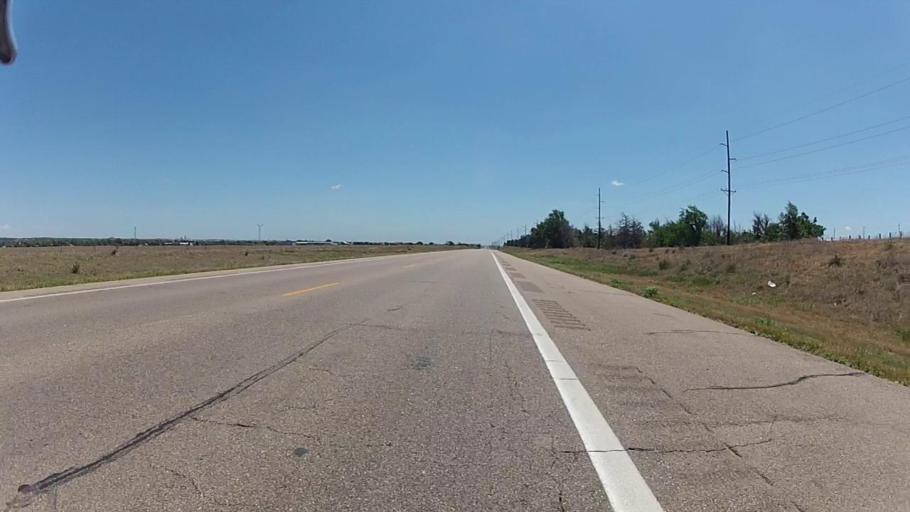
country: US
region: Kansas
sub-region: Ford County
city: Dodge City
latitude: 37.7223
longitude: -100.0429
